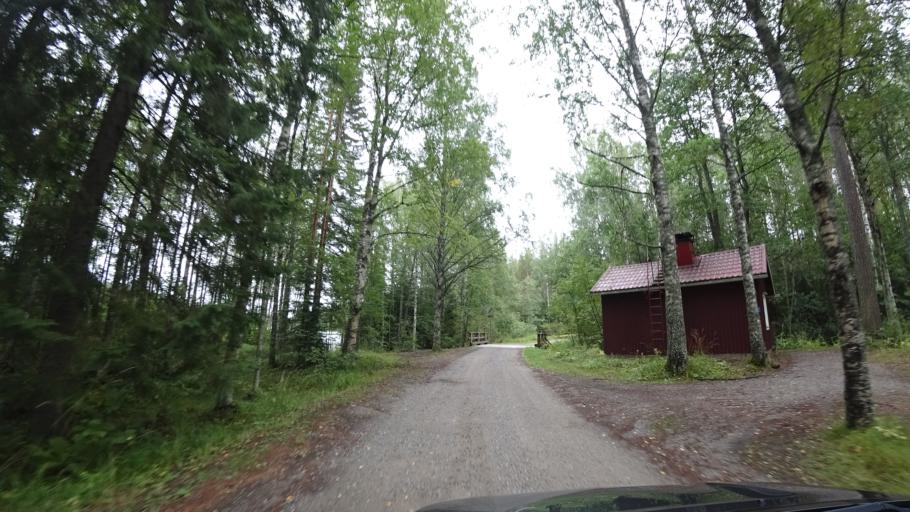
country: FI
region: Paijanne Tavastia
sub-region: Lahti
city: Auttoinen
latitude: 61.2212
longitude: 25.1433
